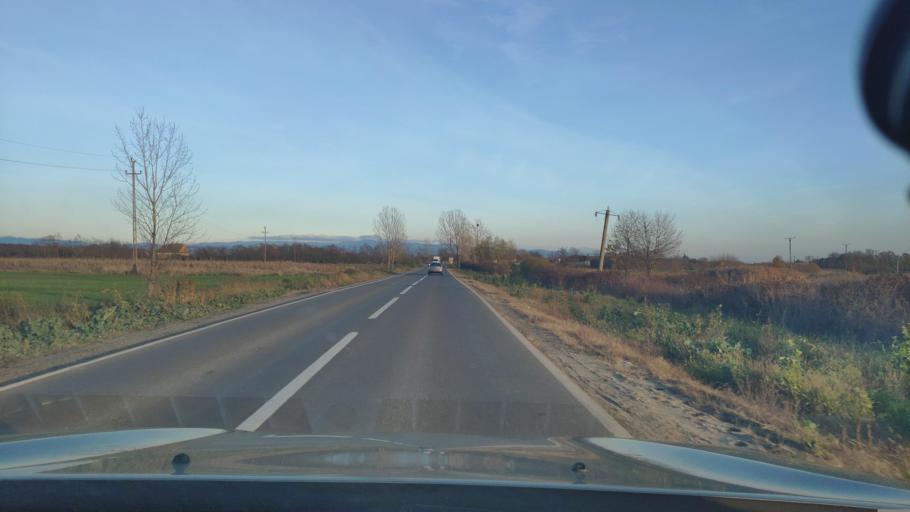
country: RO
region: Satu Mare
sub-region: Comuna Culciu
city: Caraseu
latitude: 47.7805
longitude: 23.0803
